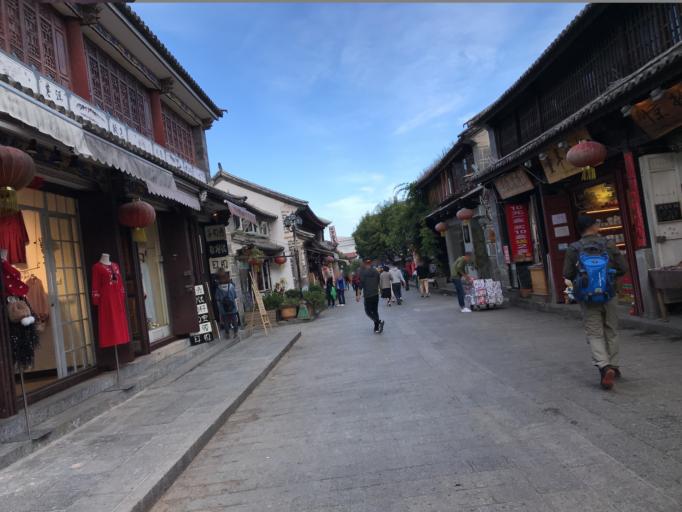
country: CN
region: Yunnan
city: Dali
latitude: 25.6976
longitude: 100.1647
